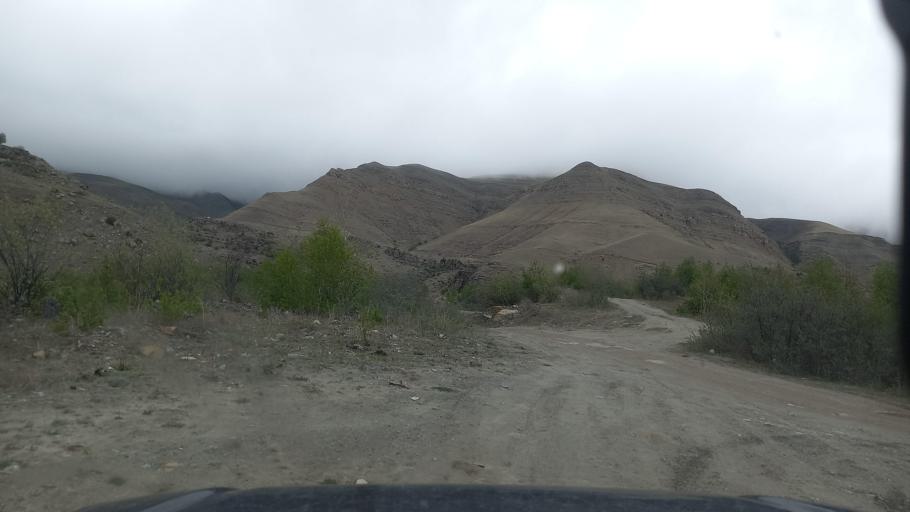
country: RU
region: Kabardino-Balkariya
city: Bylym
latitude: 43.4597
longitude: 42.9940
